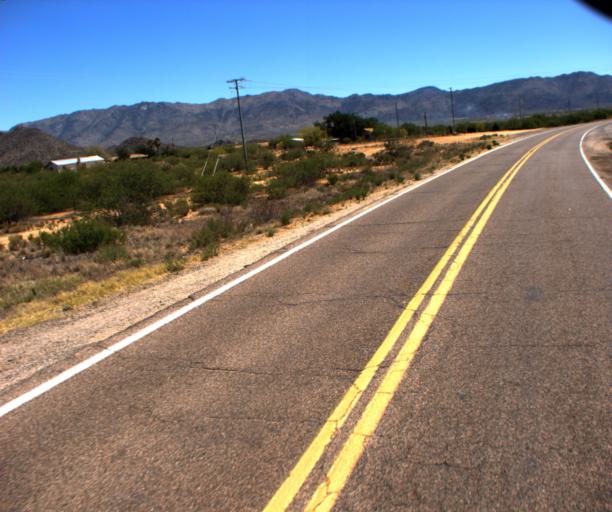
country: US
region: Arizona
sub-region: Yavapai County
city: Congress
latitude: 34.1623
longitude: -112.8524
